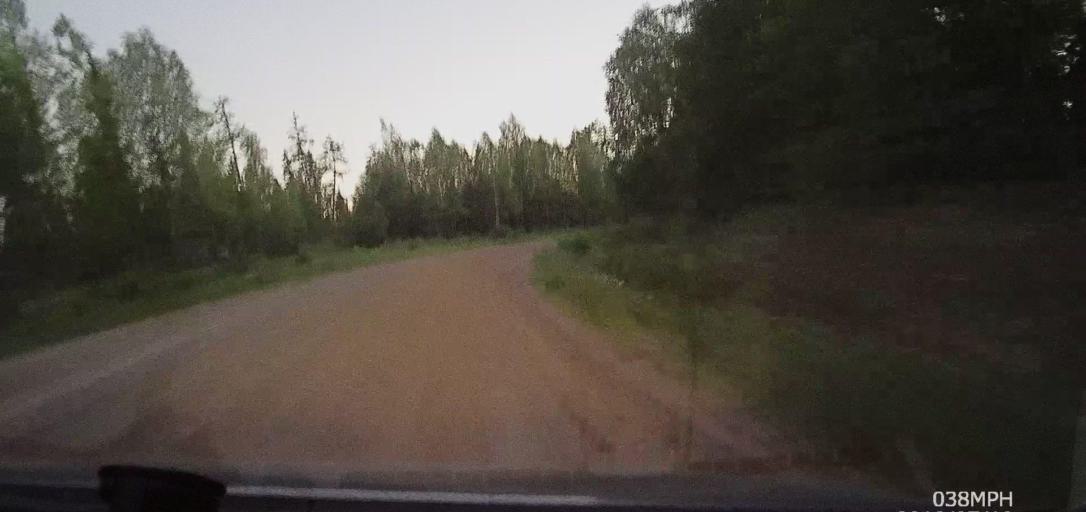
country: RU
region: Arkhangelskaya
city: Pinega
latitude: 64.4235
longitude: 43.1340
